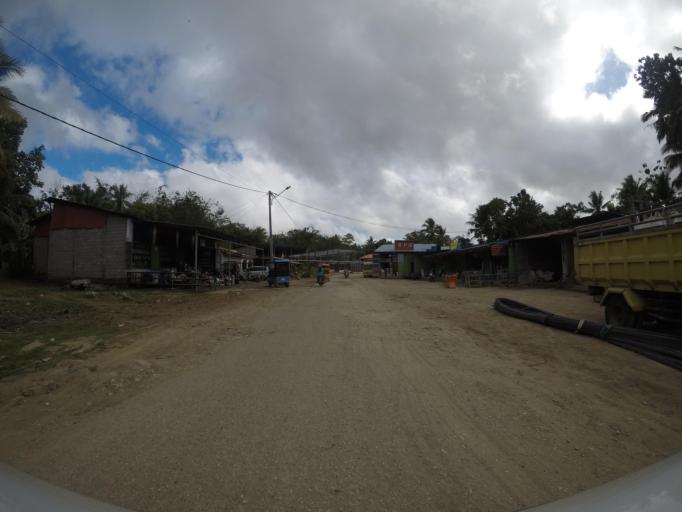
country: TL
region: Lautem
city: Lospalos
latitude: -8.5178
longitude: 126.9994
